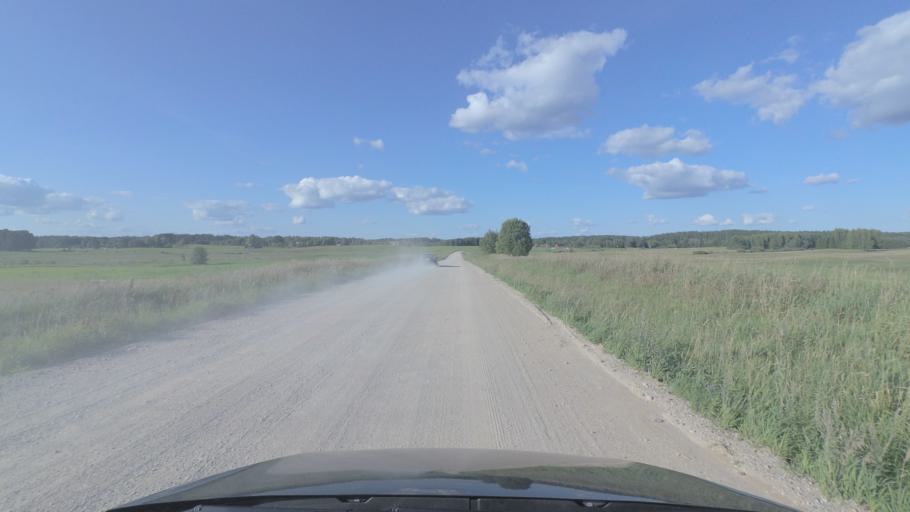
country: LT
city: Pabrade
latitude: 55.1318
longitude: 25.7064
